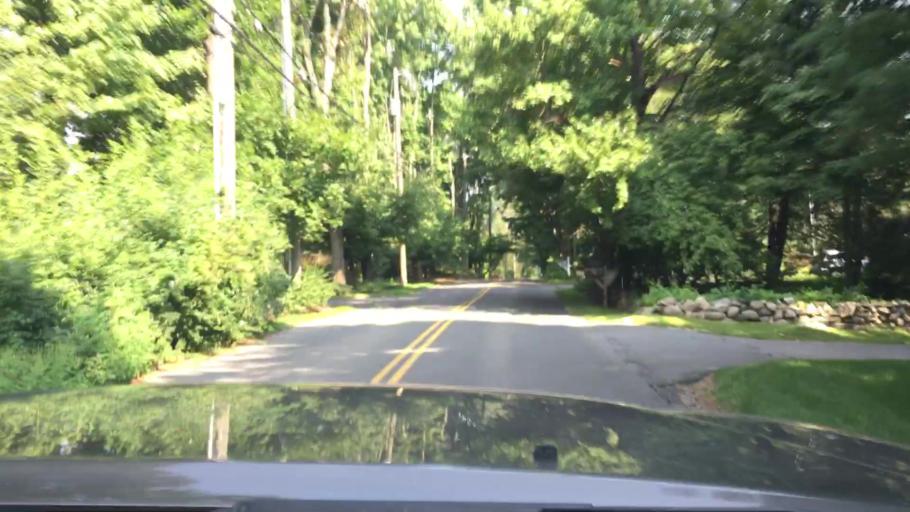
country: US
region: Connecticut
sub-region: Fairfield County
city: Georgetown
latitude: 41.2311
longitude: -73.4601
